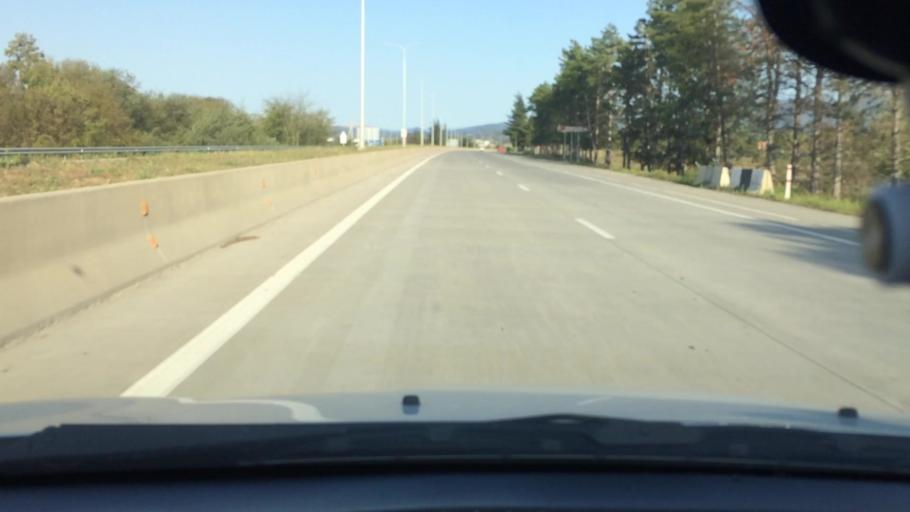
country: GE
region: Imereti
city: Zestap'oni
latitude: 42.1632
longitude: 42.9437
